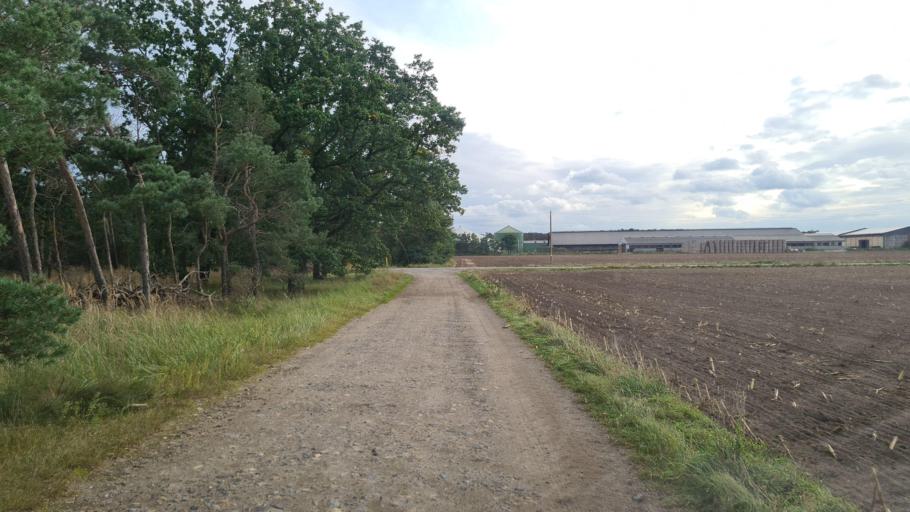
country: DE
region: Brandenburg
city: Bad Liebenwerda
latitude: 51.4679
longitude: 13.3967
